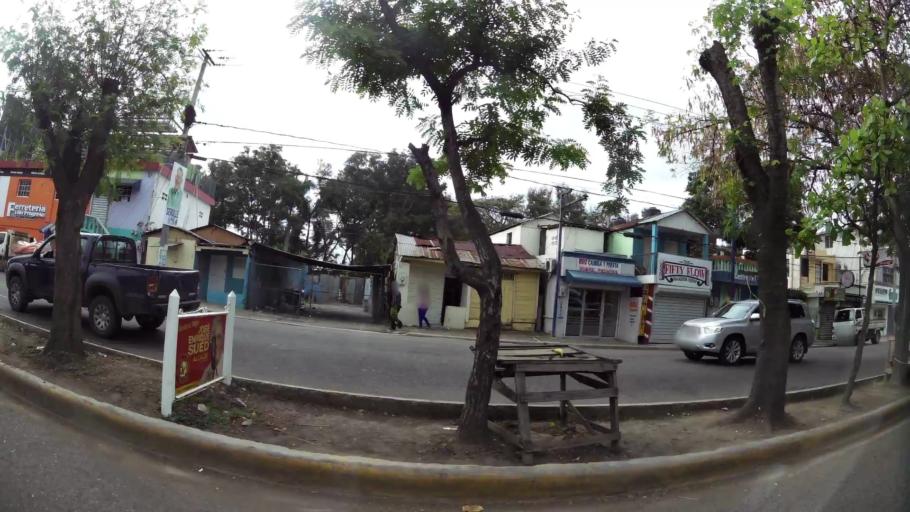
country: DO
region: Santiago
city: Santiago de los Caballeros
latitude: 19.4632
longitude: -70.6745
